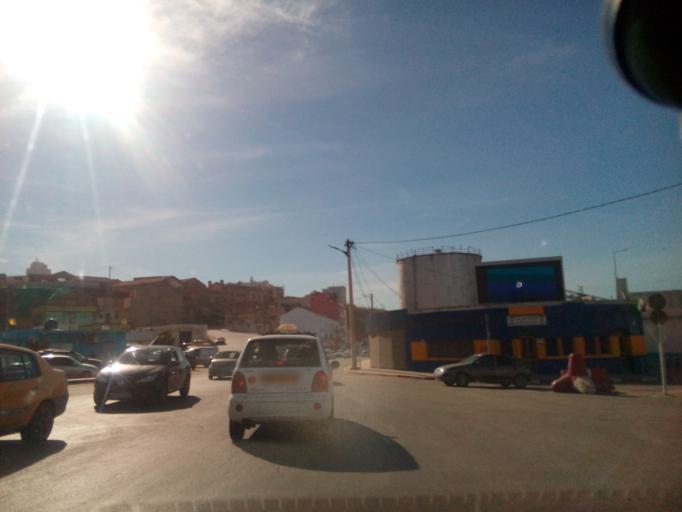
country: DZ
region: Mostaganem
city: Mostaganem
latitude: 35.9311
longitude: 0.0784
